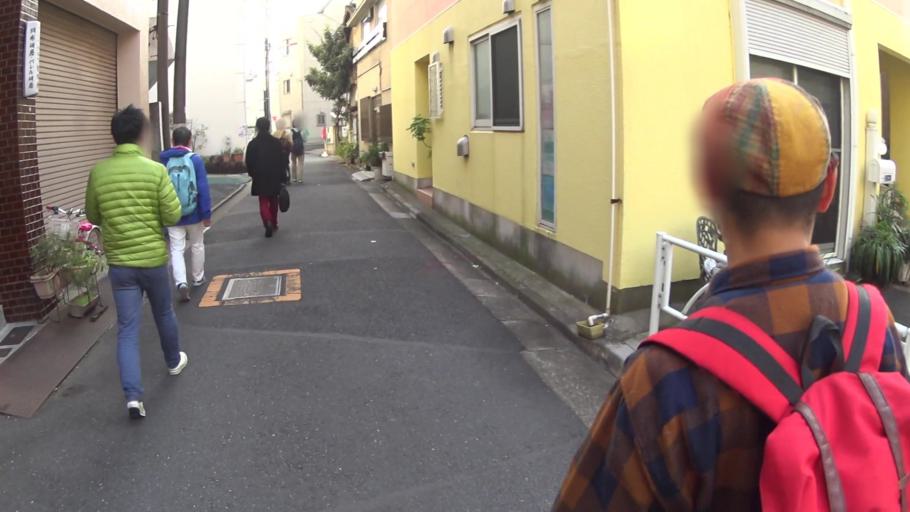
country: JP
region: Tokyo
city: Urayasu
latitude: 35.7156
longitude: 139.8145
